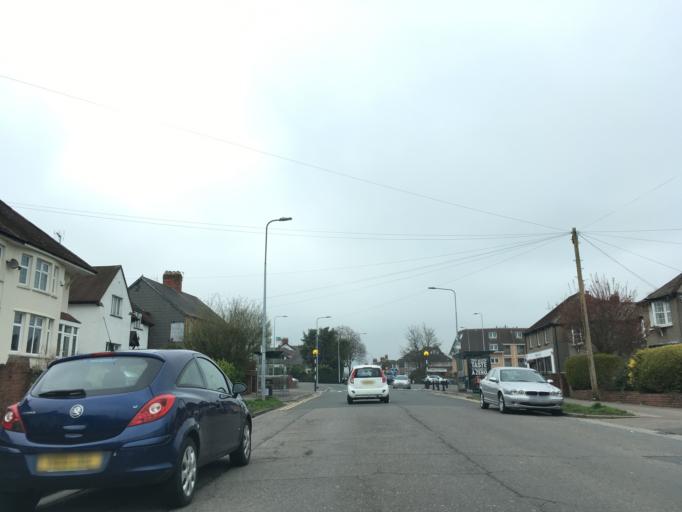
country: GB
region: Wales
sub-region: Cardiff
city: Cardiff
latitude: 51.5194
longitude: -3.1799
